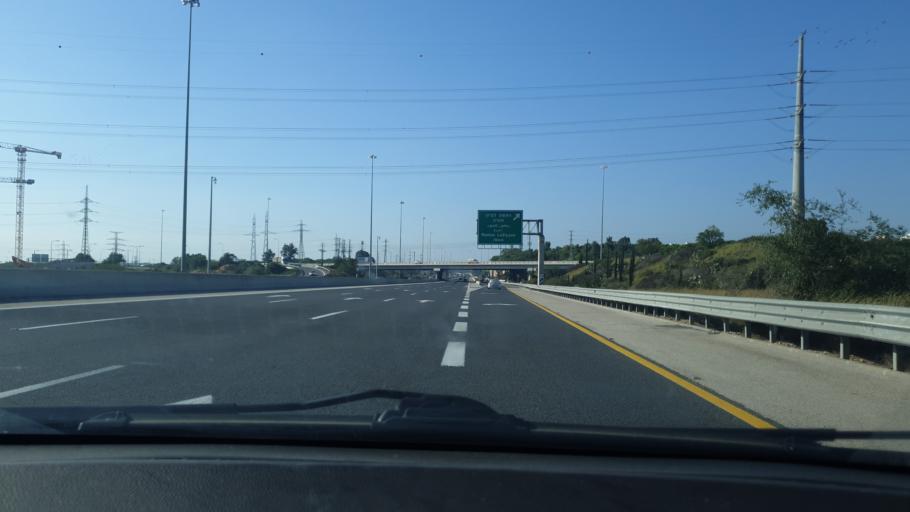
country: IL
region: Central District
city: Rishon LeZiyyon
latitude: 31.9563
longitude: 34.7780
